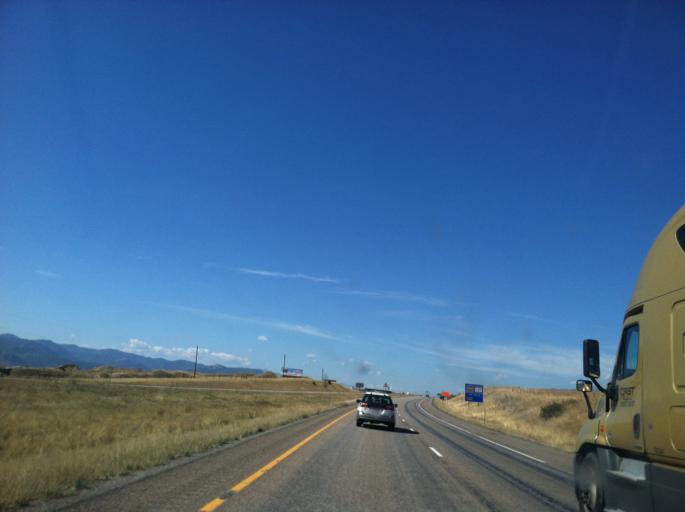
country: US
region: Montana
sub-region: Missoula County
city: Orchard Homes
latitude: 46.9410
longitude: -114.1128
